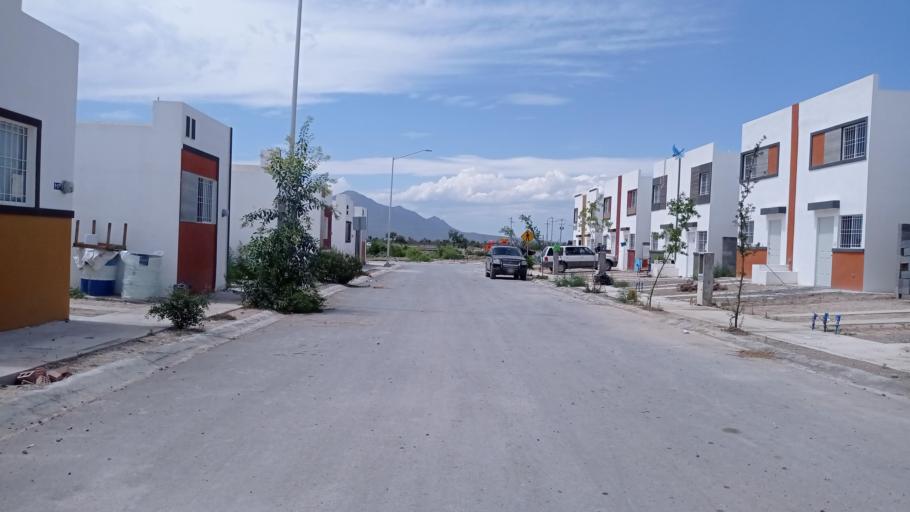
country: MX
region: Nuevo Leon
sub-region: Salinas Victoria
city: Simeprodeso (Colectivo Nuevo)
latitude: 25.8747
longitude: -100.3198
